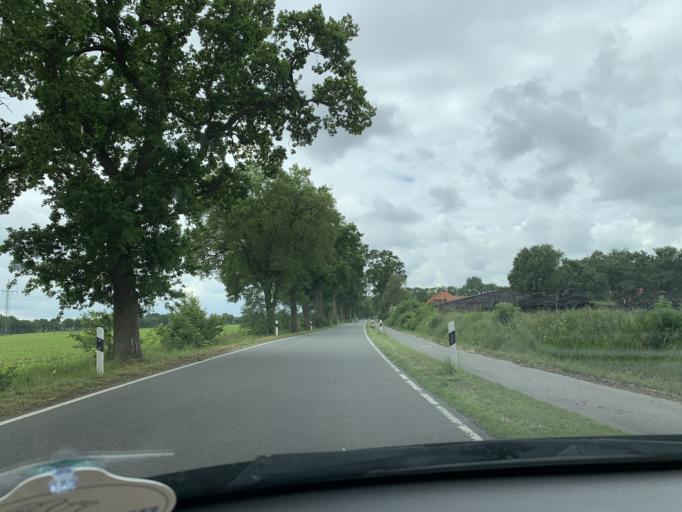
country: DE
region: Lower Saxony
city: Bockhorn
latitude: 53.3139
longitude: 8.0112
